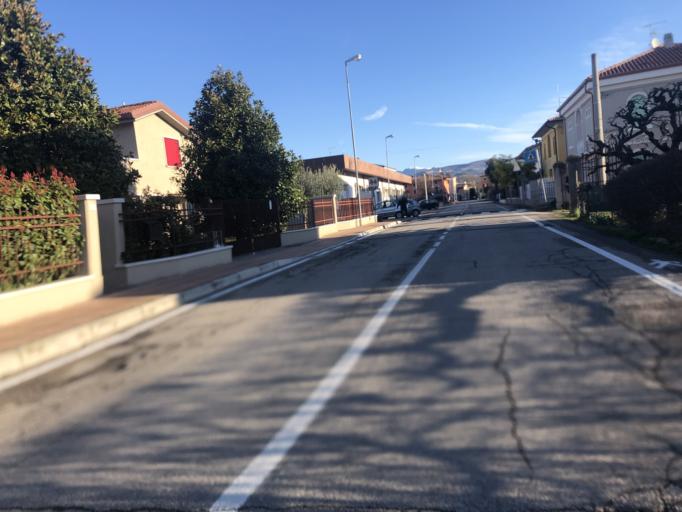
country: IT
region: Veneto
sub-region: Provincia di Verona
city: Pescantina
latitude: 45.4940
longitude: 10.8723
